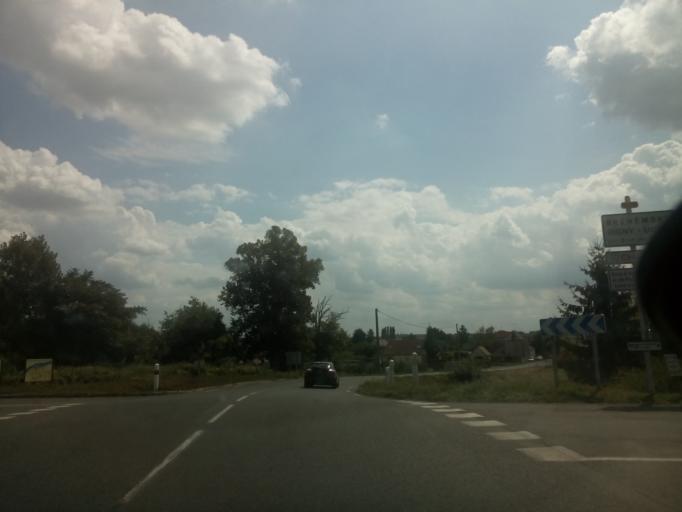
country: FR
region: Centre
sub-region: Departement d'Indre-et-Loire
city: Langeais
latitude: 47.3152
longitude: 0.4079
